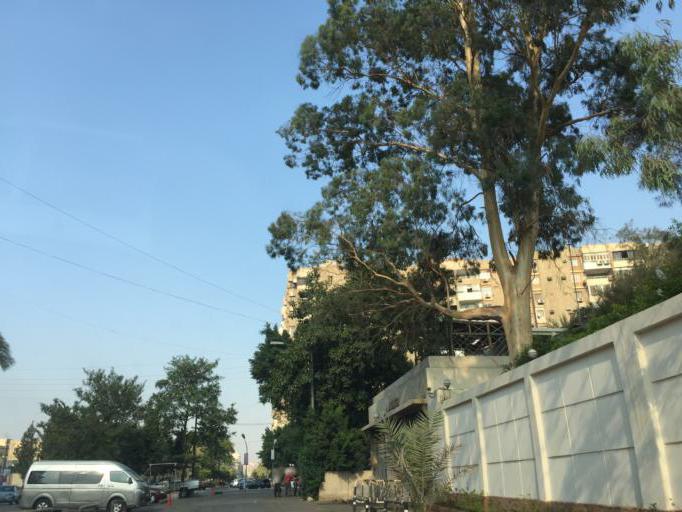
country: EG
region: Muhafazat al Qahirah
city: Cairo
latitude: 30.0797
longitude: 31.3258
